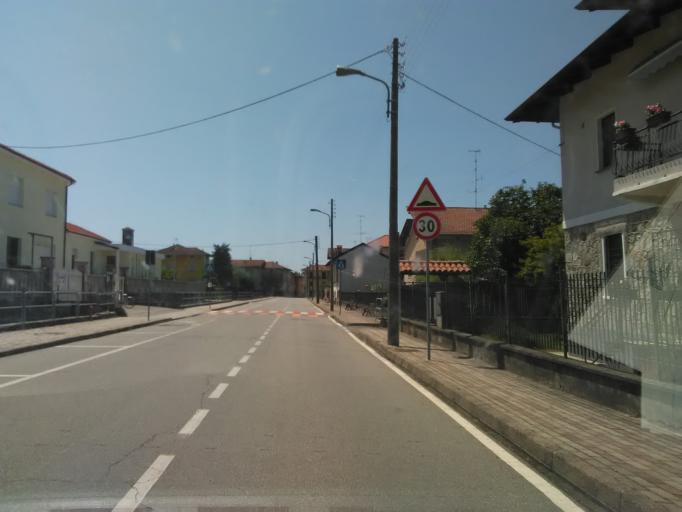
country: IT
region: Piedmont
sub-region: Provincia di Vercelli
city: Lenta
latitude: 45.5589
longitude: 8.3842
